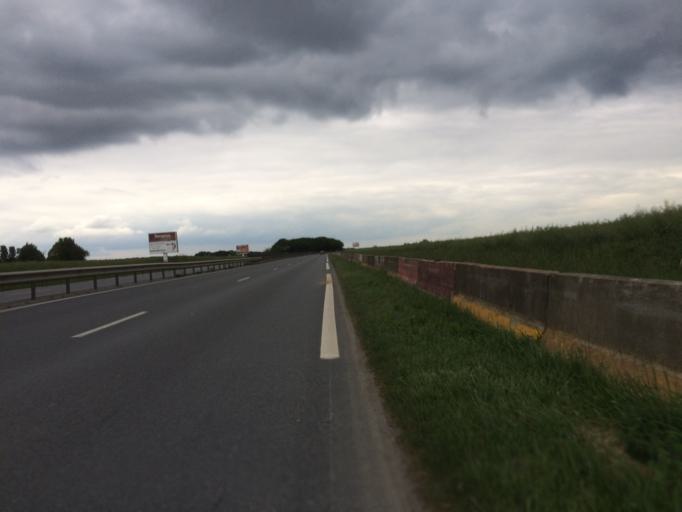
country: FR
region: Ile-de-France
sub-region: Departement de l'Essonne
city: Le Plessis-Pate
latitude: 48.6098
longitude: 2.3344
